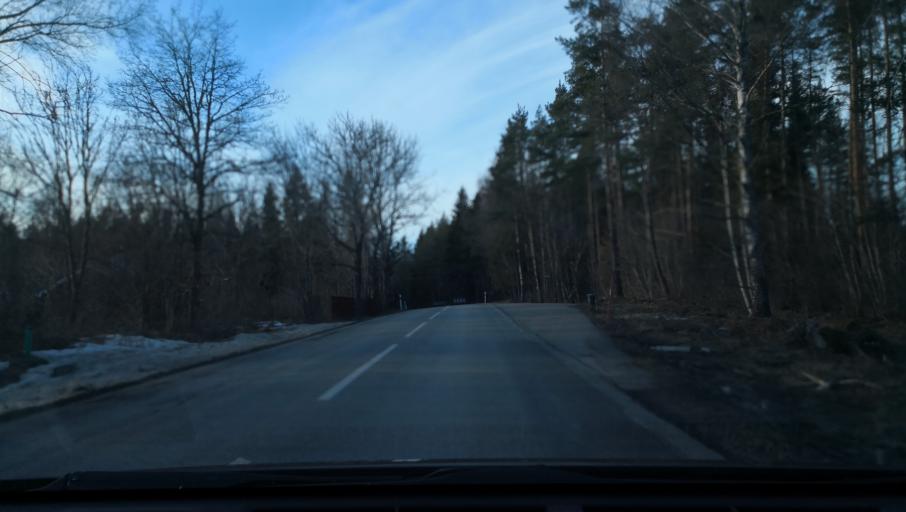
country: SE
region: Uppsala
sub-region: Osthammars Kommun
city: OEsthammar
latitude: 60.3298
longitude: 18.2377
